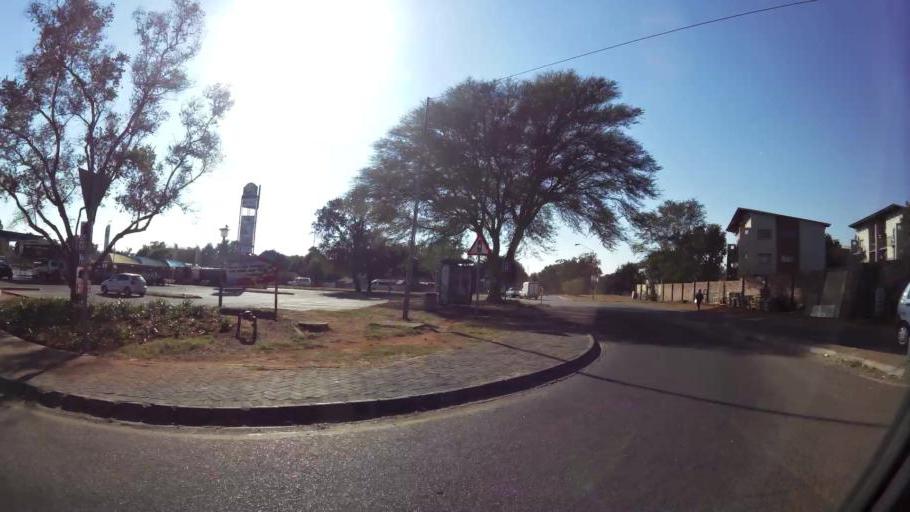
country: ZA
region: Gauteng
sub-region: City of Tshwane Metropolitan Municipality
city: Pretoria
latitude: -25.6696
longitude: 28.1556
